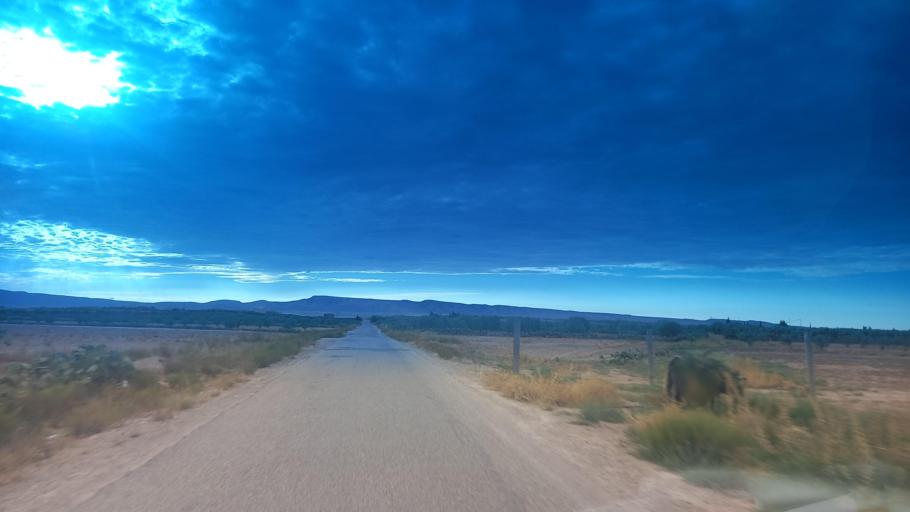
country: TN
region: Al Qasrayn
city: Sbiba
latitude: 35.3859
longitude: 9.0326
